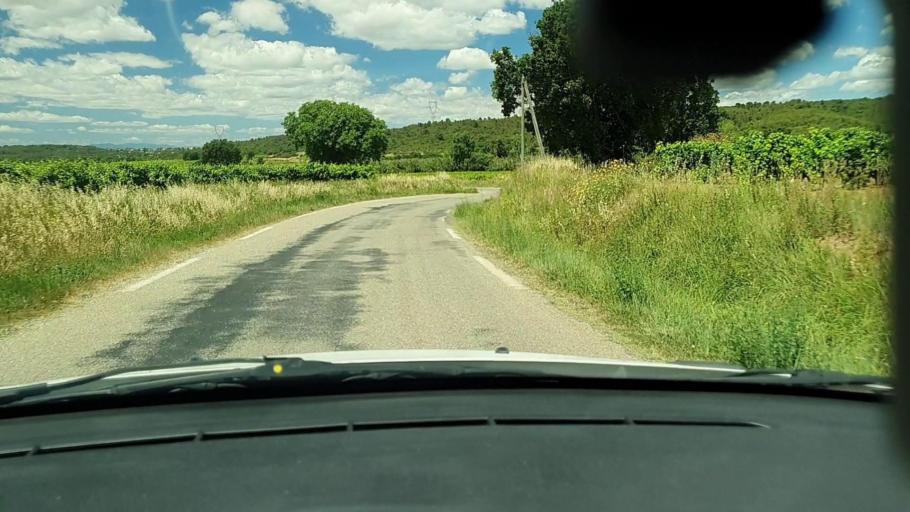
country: FR
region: Languedoc-Roussillon
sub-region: Departement du Gard
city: Poulx
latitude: 43.9522
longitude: 4.4146
